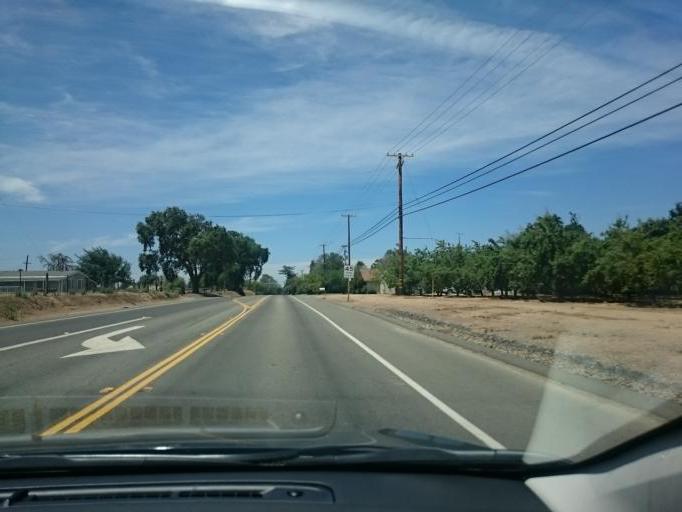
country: US
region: California
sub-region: Stanislaus County
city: Waterford
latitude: 37.6404
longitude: -120.7348
